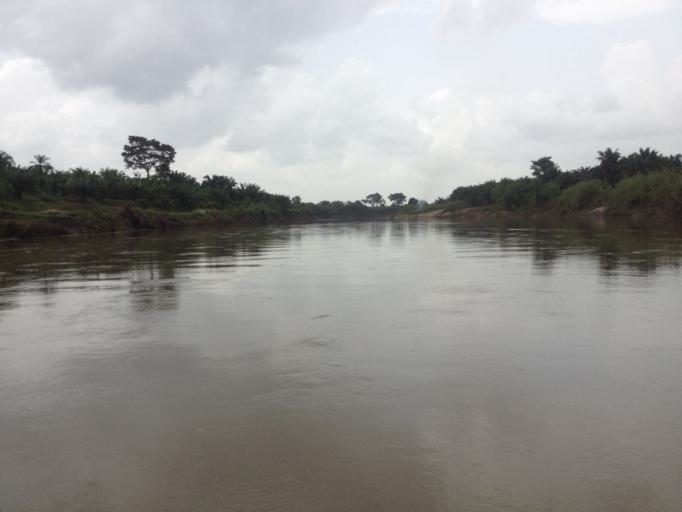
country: BJ
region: Mono
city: Lokossa
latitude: 6.5044
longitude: 1.7006
